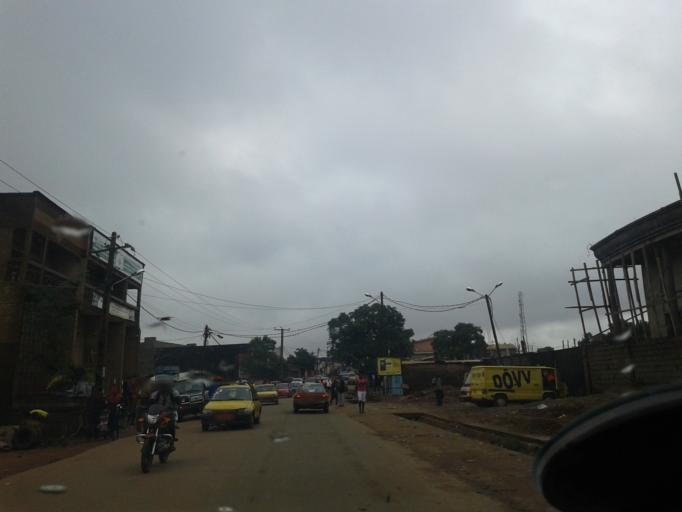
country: CM
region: Centre
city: Yaounde
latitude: 3.9084
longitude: 11.5288
